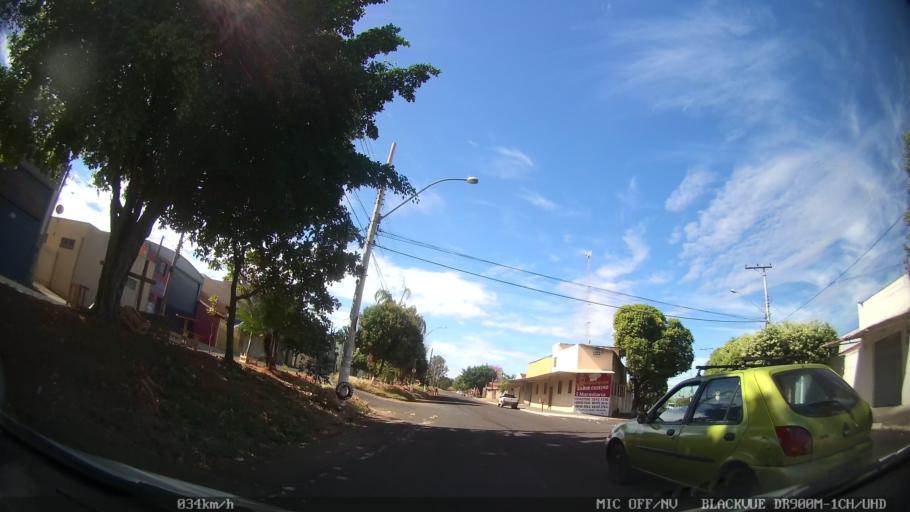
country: BR
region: Sao Paulo
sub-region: Bady Bassitt
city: Bady Bassitt
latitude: -20.8215
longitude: -49.4929
